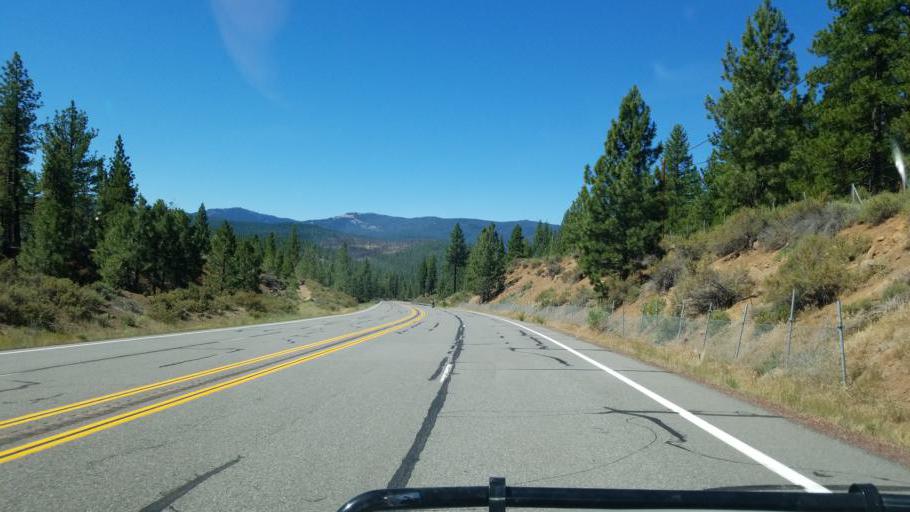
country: US
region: California
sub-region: Lassen County
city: Susanville
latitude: 40.4063
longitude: -120.7684
